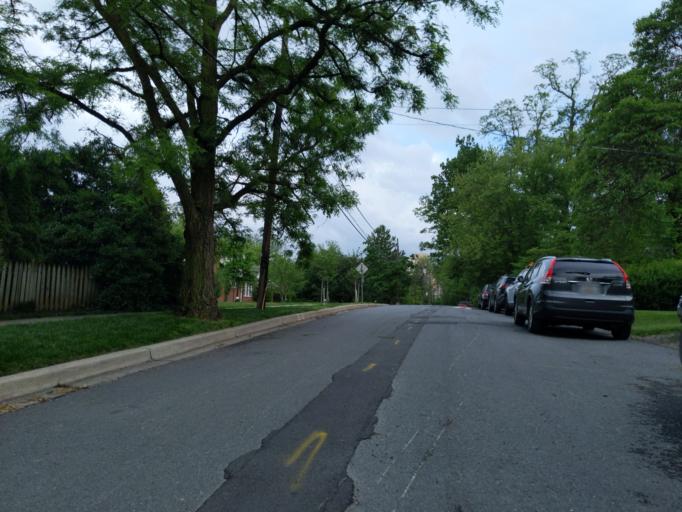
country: US
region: Maryland
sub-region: Montgomery County
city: Silver Spring
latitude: 39.0012
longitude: -77.0360
